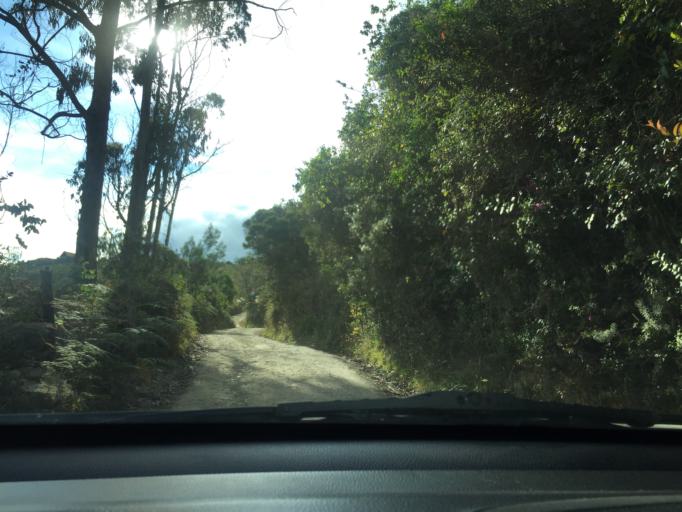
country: CO
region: Cundinamarca
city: Sopo
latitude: 4.9207
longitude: -73.9096
